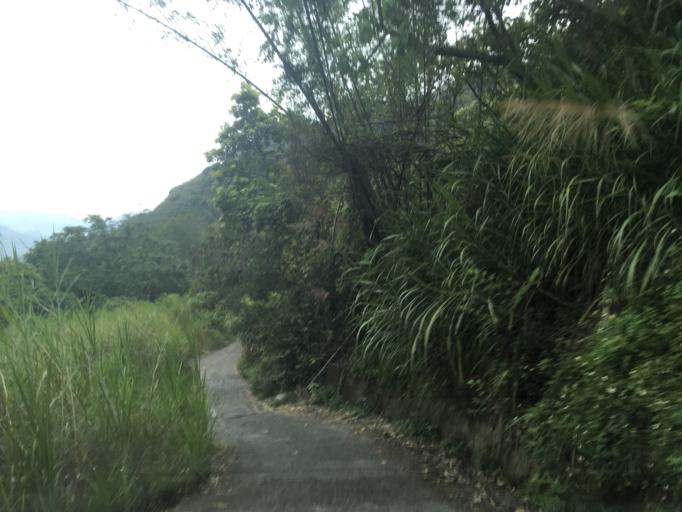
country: TW
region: Taiwan
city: Zhongxing New Village
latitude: 24.0473
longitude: 120.8056
